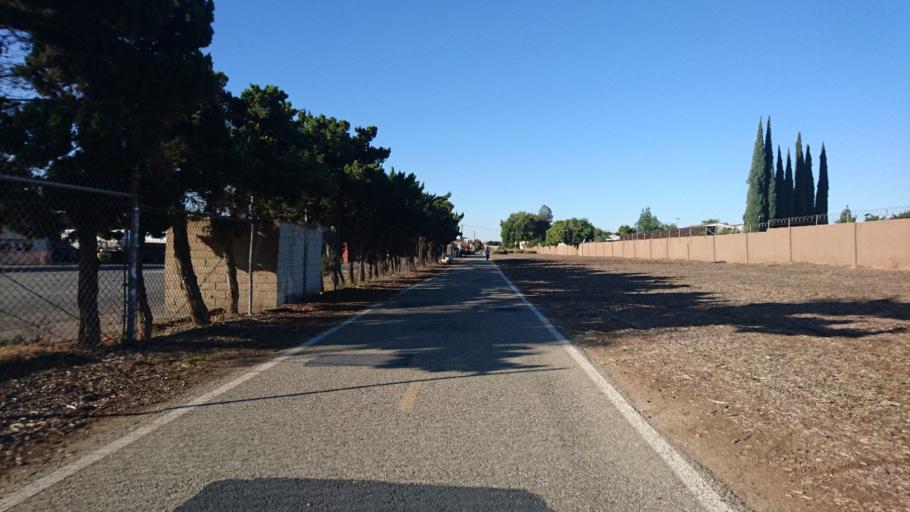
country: US
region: California
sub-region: San Bernardino County
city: Upland
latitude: 34.1006
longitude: -117.6298
